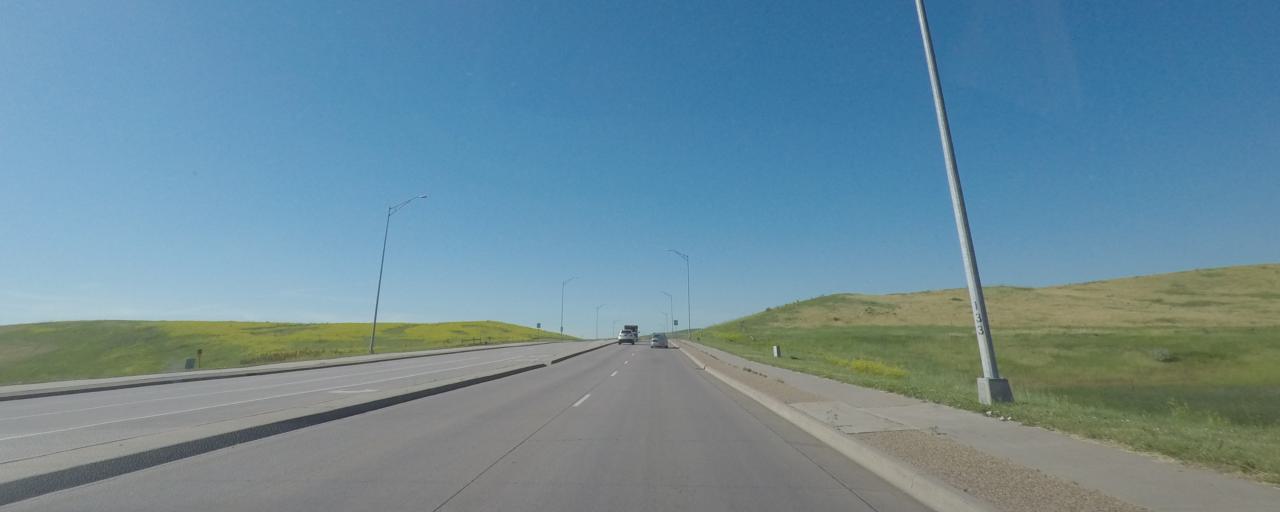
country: US
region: South Dakota
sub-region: Pennington County
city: Rapid City
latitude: 44.0424
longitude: -103.2192
